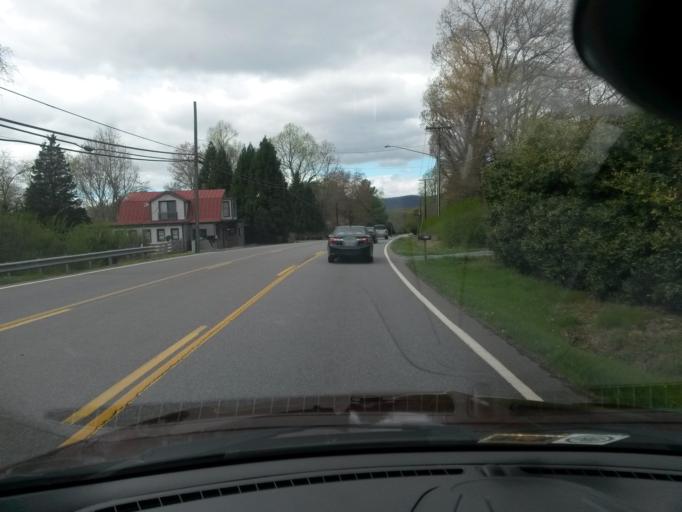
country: US
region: Virginia
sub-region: City of Lynchburg
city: West Lynchburg
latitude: 37.4419
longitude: -79.2368
